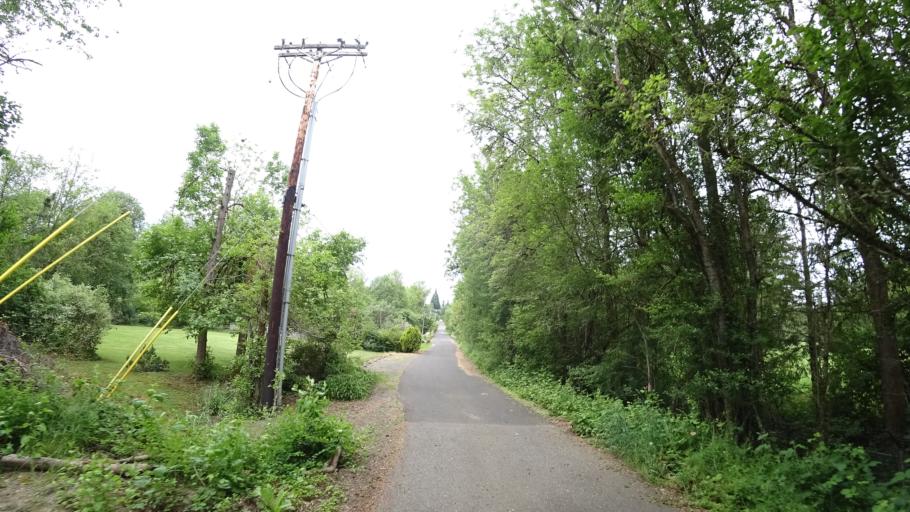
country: US
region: Oregon
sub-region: Washington County
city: Garden Home-Whitford
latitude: 45.4701
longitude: -122.7653
